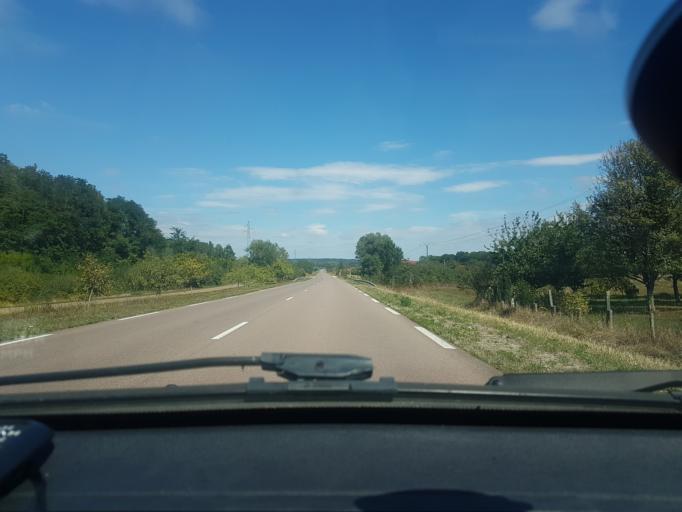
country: FR
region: Franche-Comte
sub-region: Departement de la Haute-Saone
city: Gray-la-Ville
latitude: 47.4197
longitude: 5.5211
